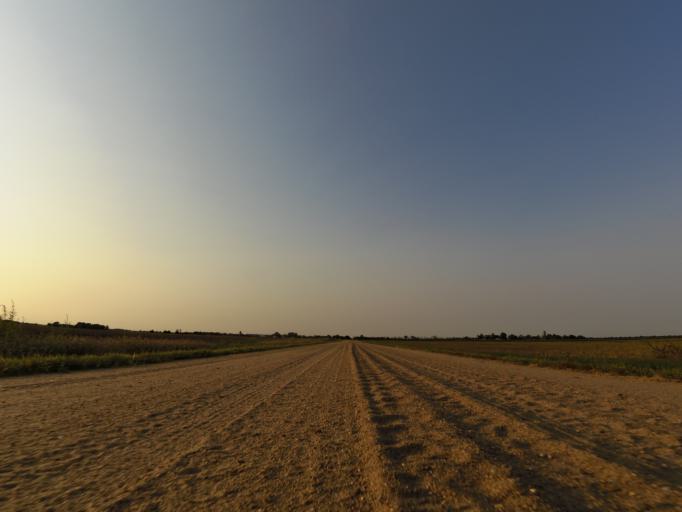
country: US
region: Kansas
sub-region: Reno County
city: South Hutchinson
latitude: 37.9771
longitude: -97.9957
